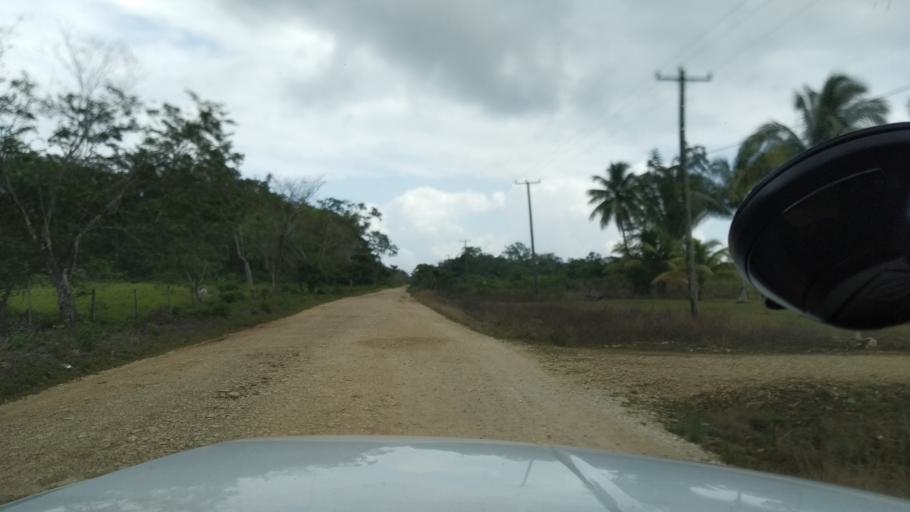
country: BZ
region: Toledo
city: Punta Gorda
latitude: 16.2165
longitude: -89.0059
